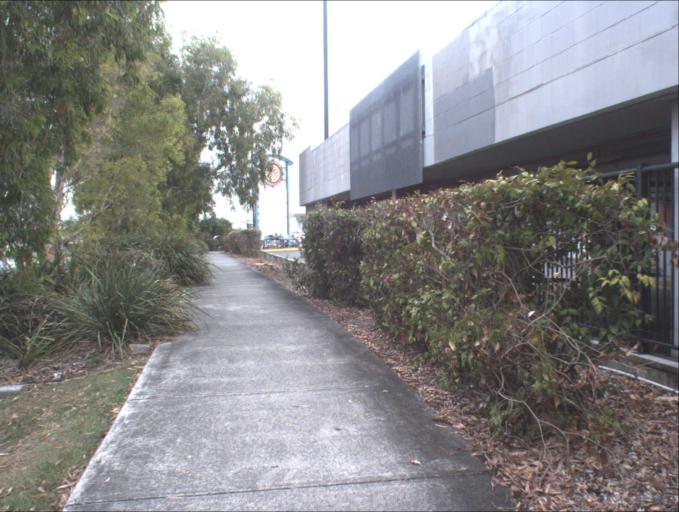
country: AU
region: Queensland
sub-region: Logan
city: Rochedale South
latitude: -27.6075
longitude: 153.1110
